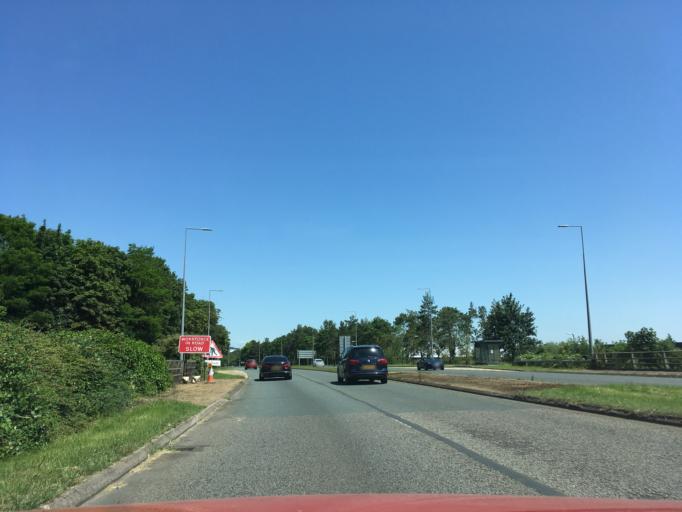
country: GB
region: England
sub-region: Milton Keynes
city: Loughton
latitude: 52.0232
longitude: -0.7769
